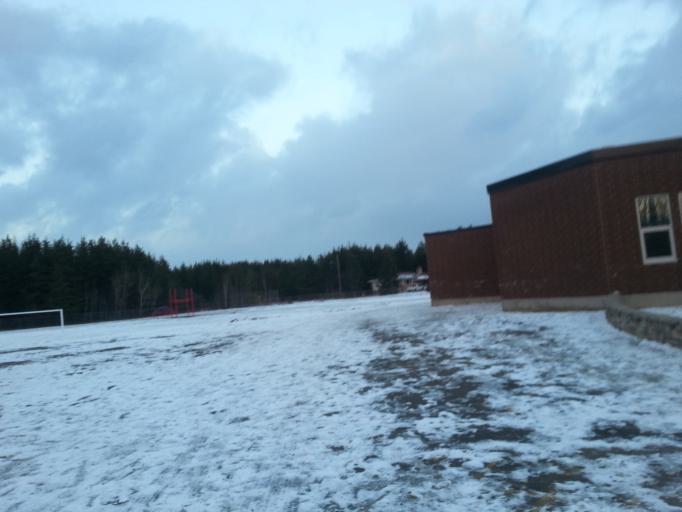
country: CA
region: Ontario
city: Greater Sudbury
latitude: 46.6541
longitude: -80.9399
